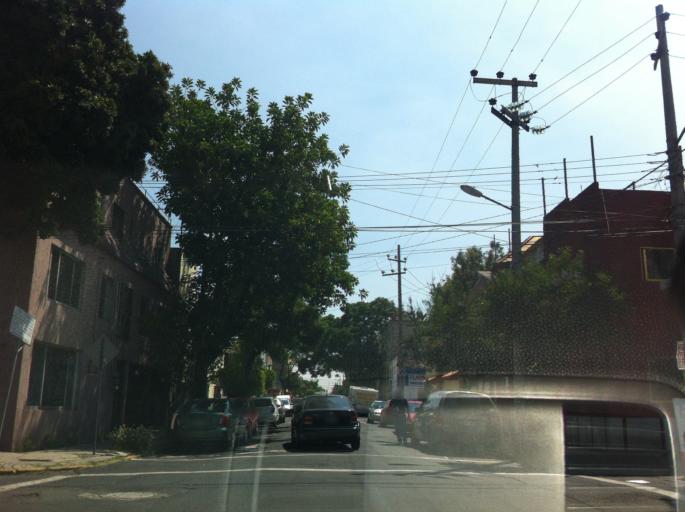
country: MX
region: Mexico City
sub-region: Iztacalco
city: Iztacalco
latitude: 19.4176
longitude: -99.0970
